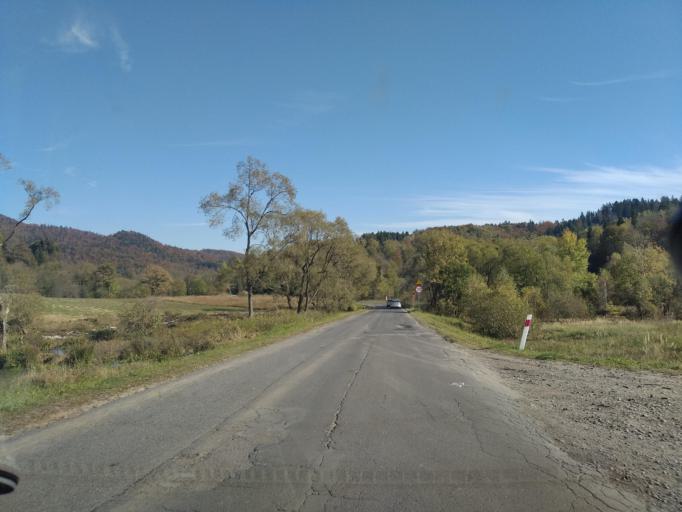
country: PL
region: Subcarpathian Voivodeship
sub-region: Powiat leski
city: Cisna
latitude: 49.2066
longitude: 22.2571
